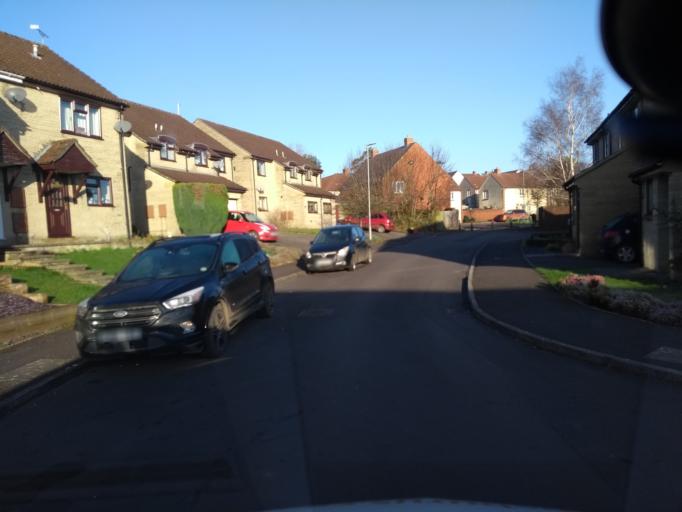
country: GB
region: England
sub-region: Somerset
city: Bruton
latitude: 51.1181
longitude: -2.4480
